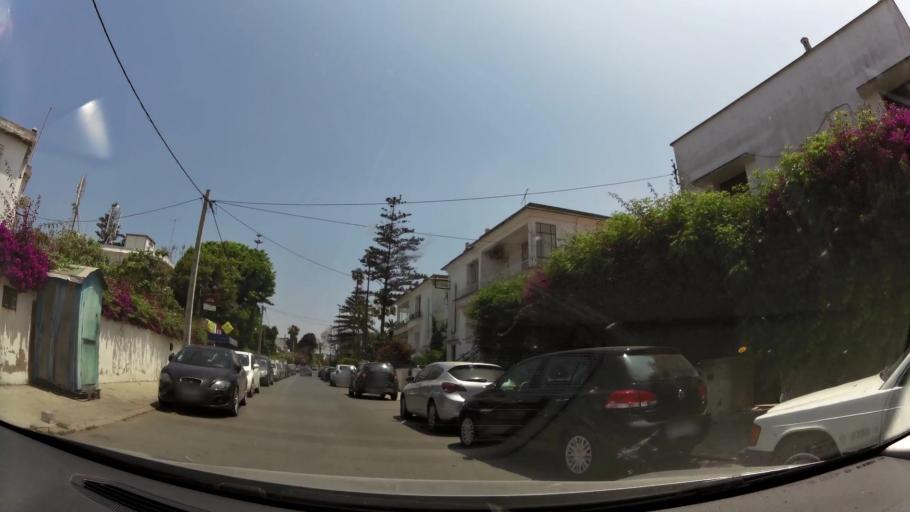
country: MA
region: Rabat-Sale-Zemmour-Zaer
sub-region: Rabat
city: Rabat
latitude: 34.0137
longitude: -6.8413
